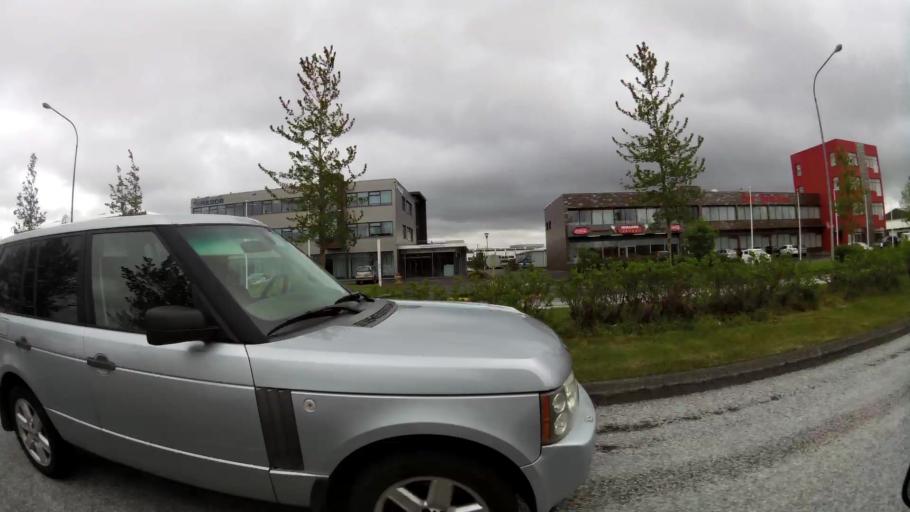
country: IS
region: Capital Region
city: Hafnarfjoerdur
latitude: 64.0809
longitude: -21.9486
